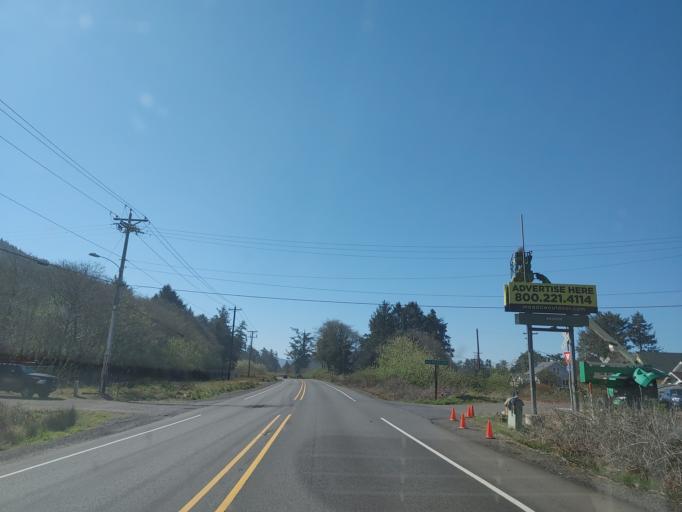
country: US
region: Oregon
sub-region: Tillamook County
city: Rockaway Beach
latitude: 45.5882
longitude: -123.9479
